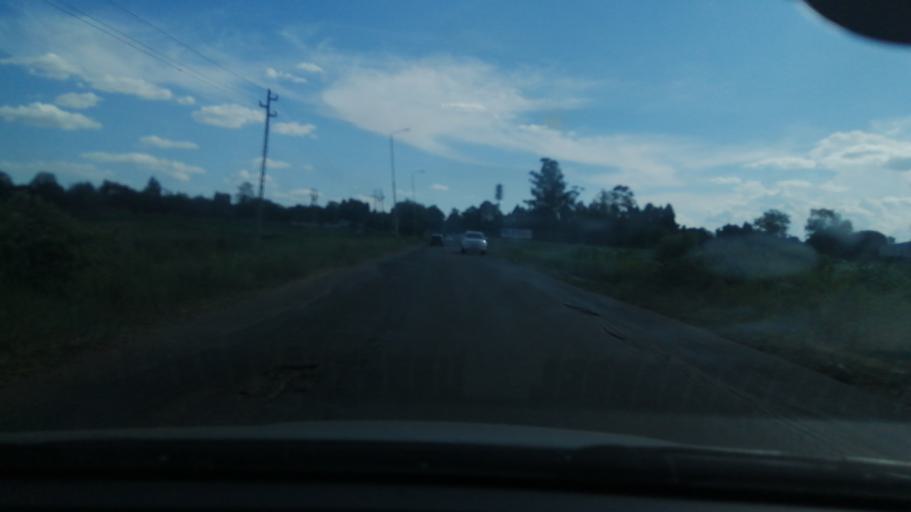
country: ZW
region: Harare
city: Harare
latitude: -17.7728
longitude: 31.0686
